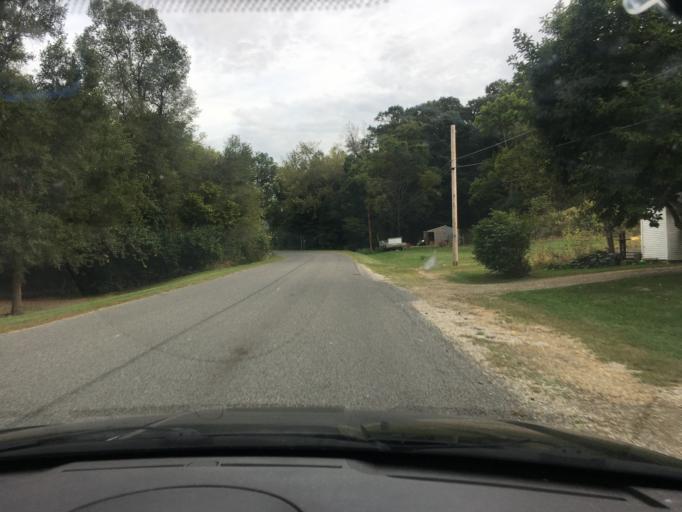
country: US
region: Ohio
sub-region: Logan County
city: West Liberty
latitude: 40.3025
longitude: -83.6999
